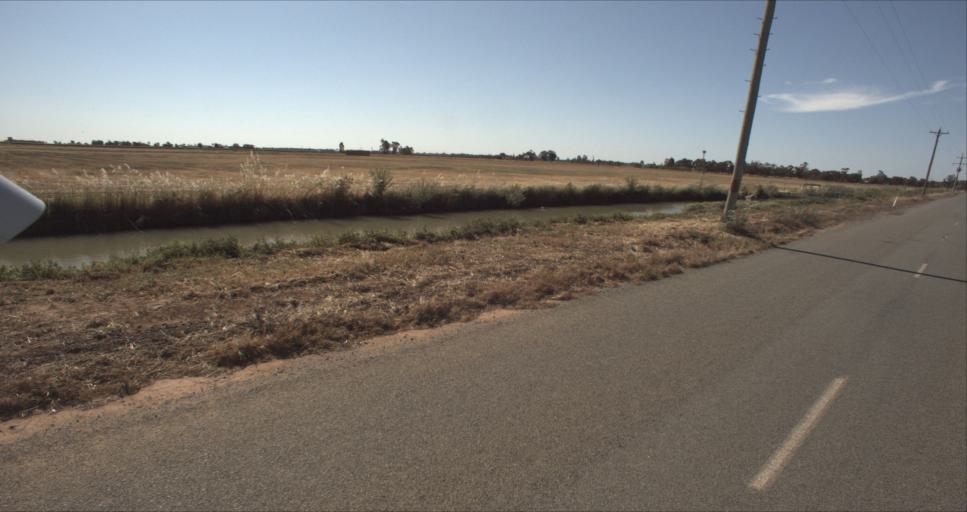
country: AU
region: New South Wales
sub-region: Leeton
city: Leeton
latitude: -34.5757
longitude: 146.3808
